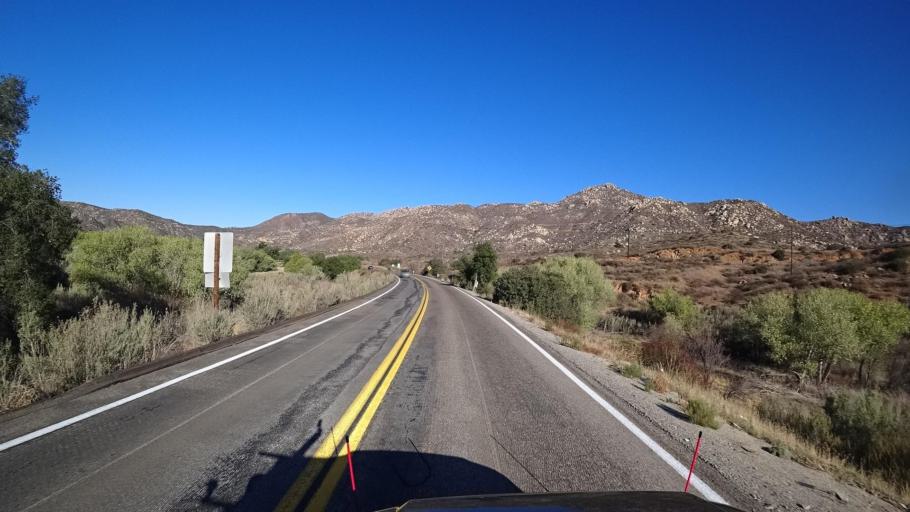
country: MX
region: Baja California
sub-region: Tecate
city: Lomas de Santa Anita
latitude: 32.6094
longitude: -116.7010
